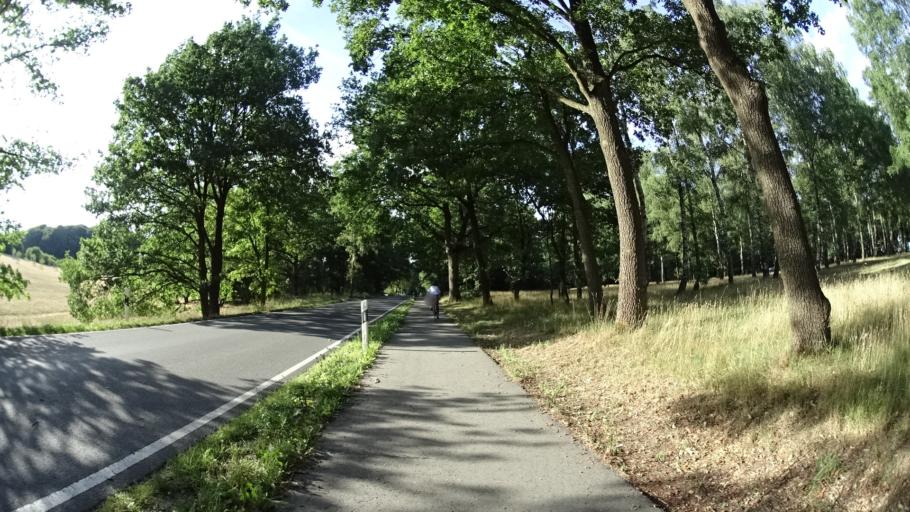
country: DE
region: Lower Saxony
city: Undeloh
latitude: 53.1512
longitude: 9.9076
